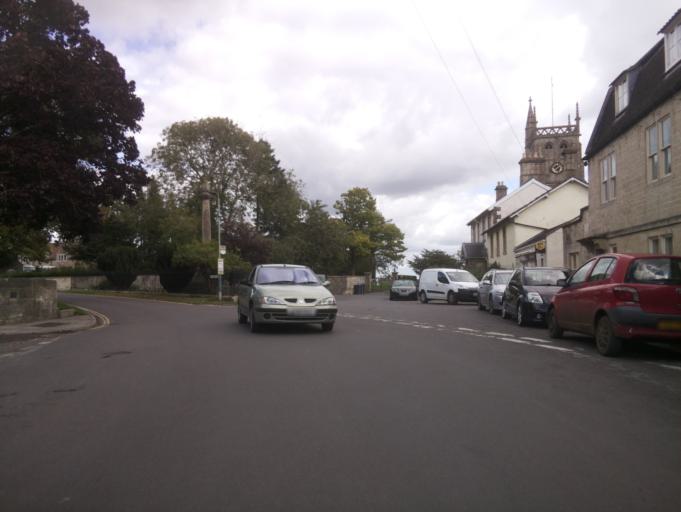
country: GB
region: England
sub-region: Wiltshire
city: Colerne
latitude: 51.4389
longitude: -2.2604
